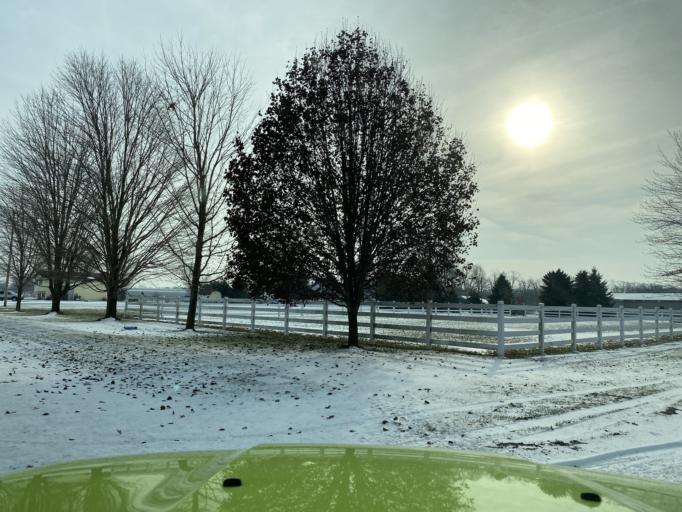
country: US
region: Michigan
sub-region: Ottawa County
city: Allendale
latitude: 42.9577
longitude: -85.9502
